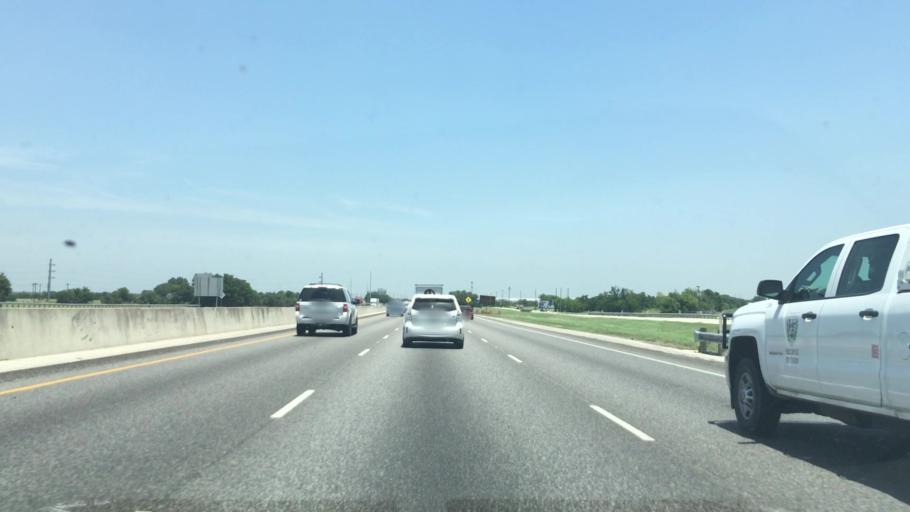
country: US
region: Texas
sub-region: Hays County
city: San Marcos
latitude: 29.9134
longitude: -97.8974
